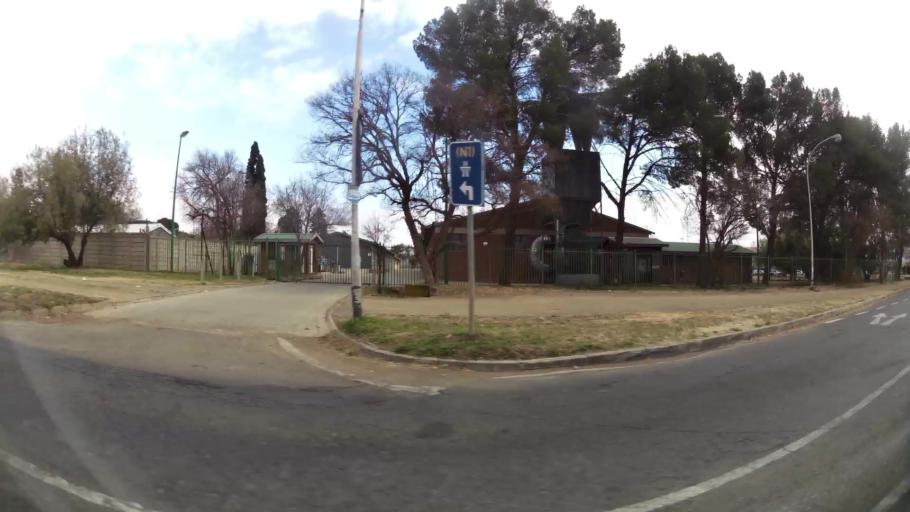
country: ZA
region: Orange Free State
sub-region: Mangaung Metropolitan Municipality
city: Bloemfontein
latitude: -29.1060
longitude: 26.1879
